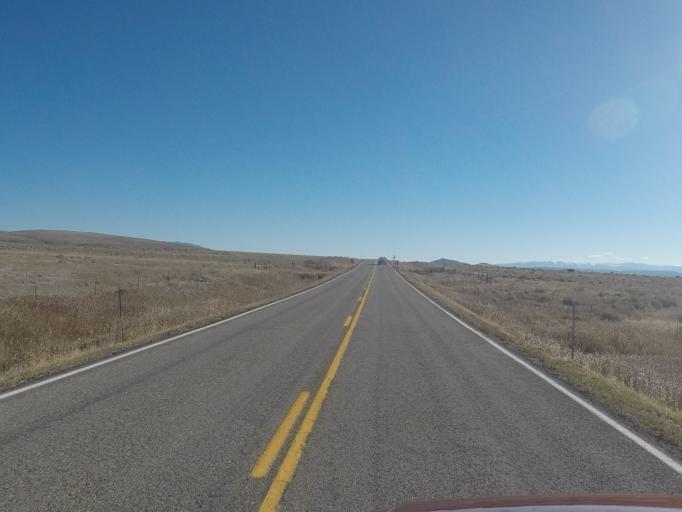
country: US
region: Montana
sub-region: Meagher County
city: White Sulphur Springs
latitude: 46.3535
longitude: -111.0454
